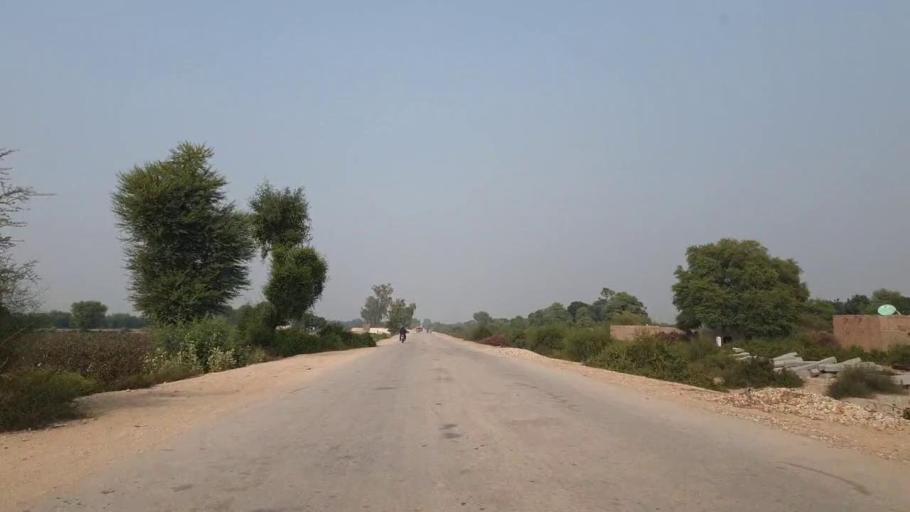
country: PK
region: Sindh
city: Bhan
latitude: 26.5783
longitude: 67.7281
